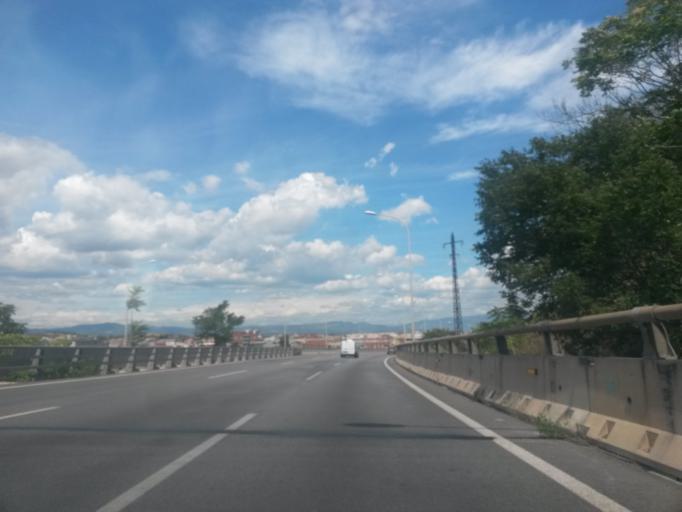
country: ES
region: Catalonia
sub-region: Provincia de Barcelona
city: Montcada i Reixac
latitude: 41.4859
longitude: 2.1843
